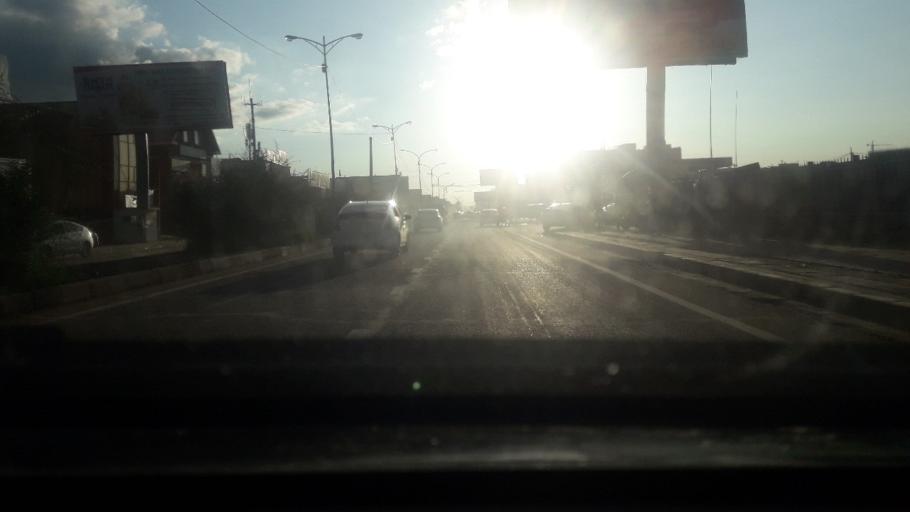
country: MN
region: Ulaanbaatar
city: Ulaanbaatar
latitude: 47.9080
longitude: 106.9532
